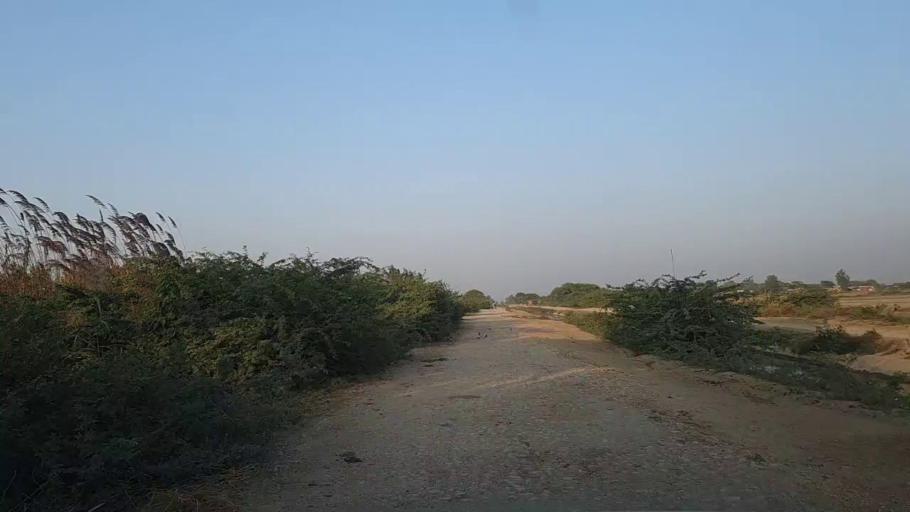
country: PK
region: Sindh
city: Mirpur Sakro
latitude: 24.2880
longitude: 67.6917
